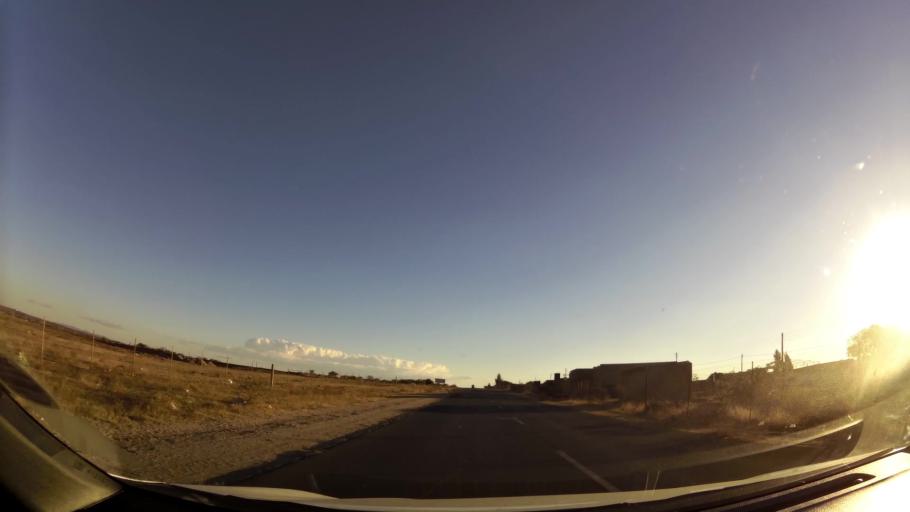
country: ZA
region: Limpopo
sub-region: Capricorn District Municipality
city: Polokwane
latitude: -23.8324
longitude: 29.3699
